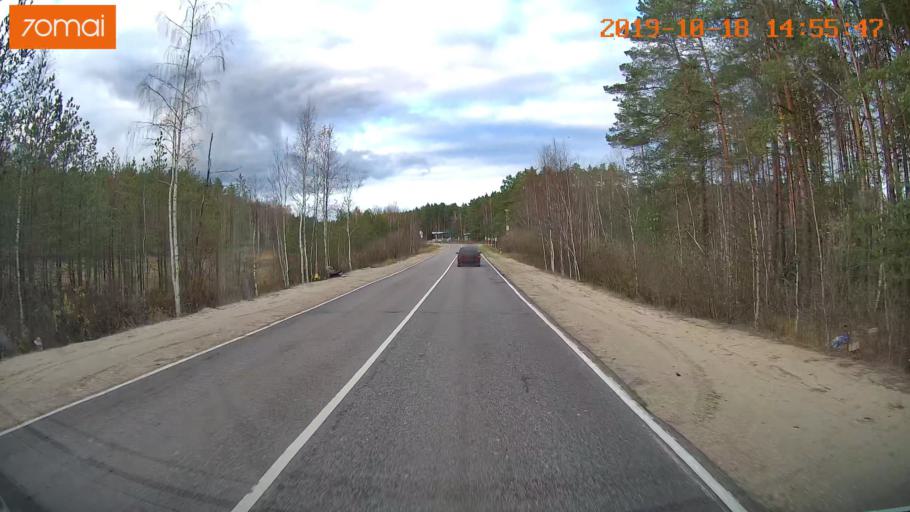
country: RU
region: Vladimir
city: Kurlovo
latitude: 55.4570
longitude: 40.5896
